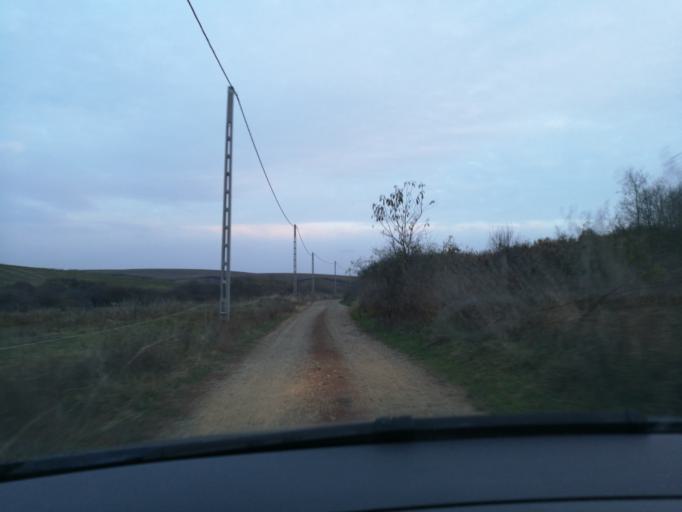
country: HU
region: Nograd
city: Bujak
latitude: 47.8658
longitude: 19.5621
